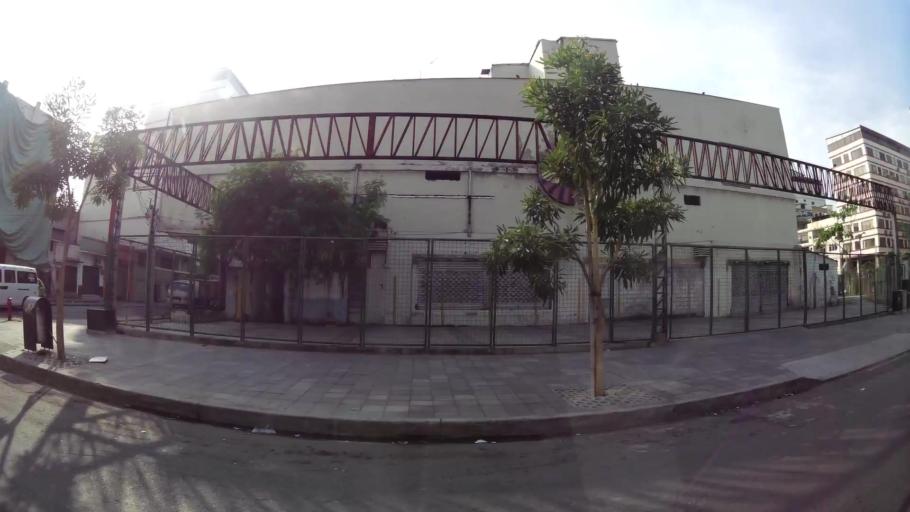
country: EC
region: Guayas
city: Guayaquil
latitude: -2.1890
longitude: -79.8852
